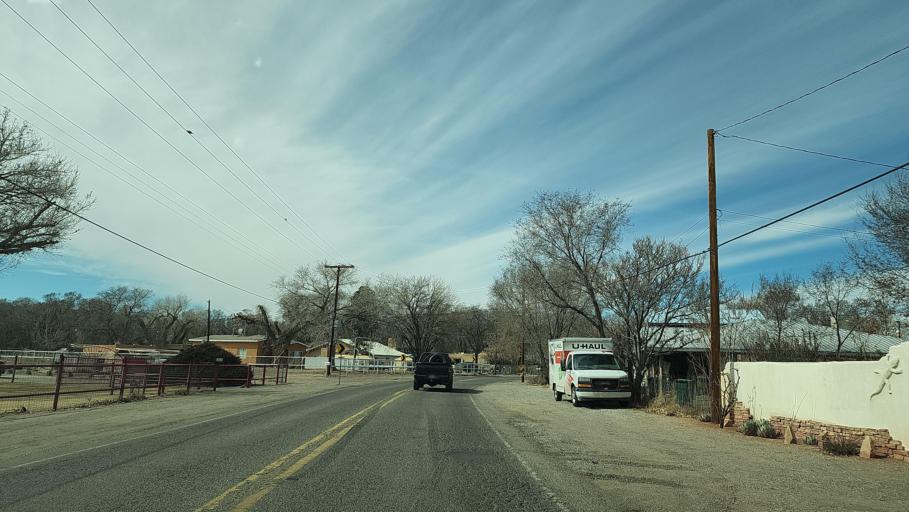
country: US
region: New Mexico
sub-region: Bernalillo County
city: South Valley
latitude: 35.0361
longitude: -106.7021
